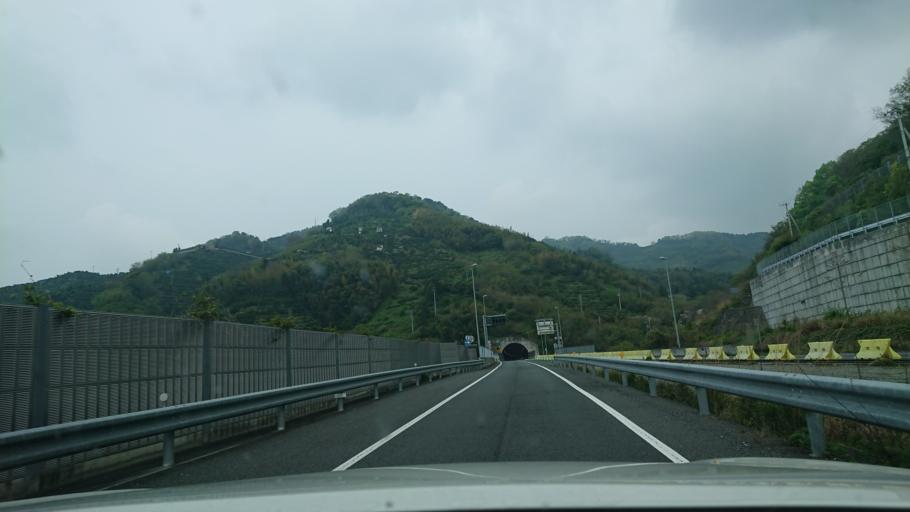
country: JP
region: Ehime
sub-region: Nishiuwa-gun
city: Ikata-cho
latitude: 33.4690
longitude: 132.4259
